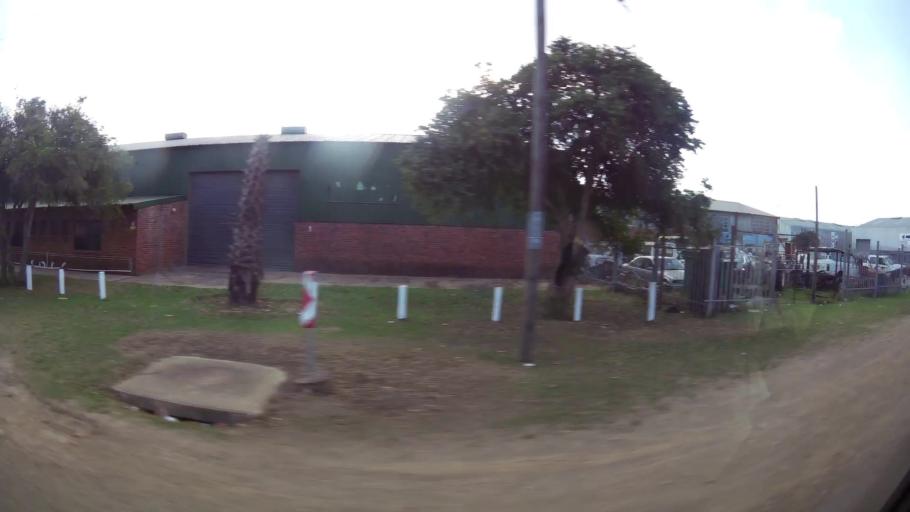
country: ZA
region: Eastern Cape
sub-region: Nelson Mandela Bay Metropolitan Municipality
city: Uitenhage
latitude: -33.7708
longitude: 25.3911
